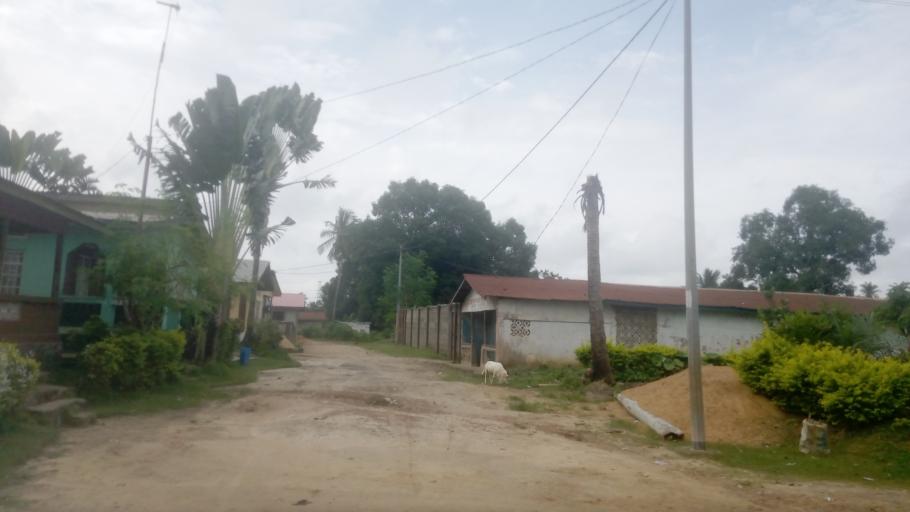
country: SL
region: Northern Province
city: Lunsar
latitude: 8.6886
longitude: -12.5384
